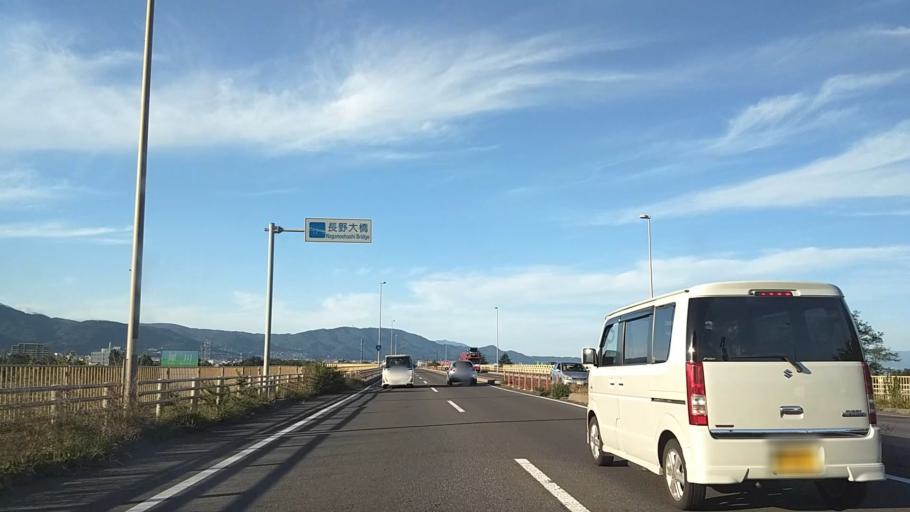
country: JP
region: Nagano
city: Nagano-shi
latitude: 36.6167
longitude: 138.1980
